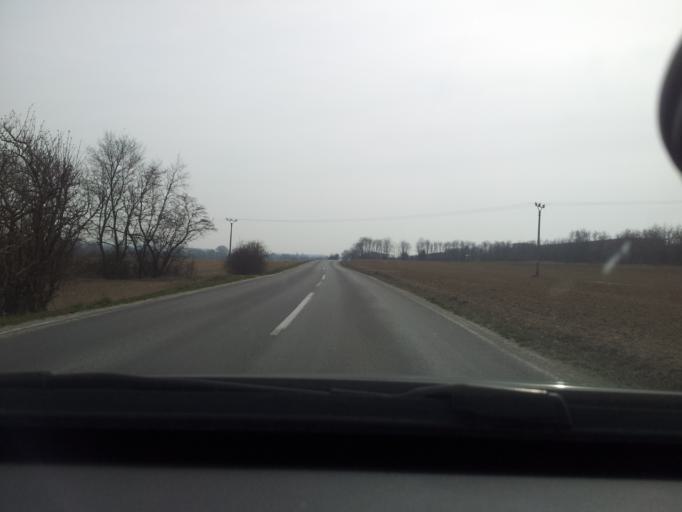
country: SK
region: Trnavsky
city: Hlohovec
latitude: 48.3812
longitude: 17.8724
